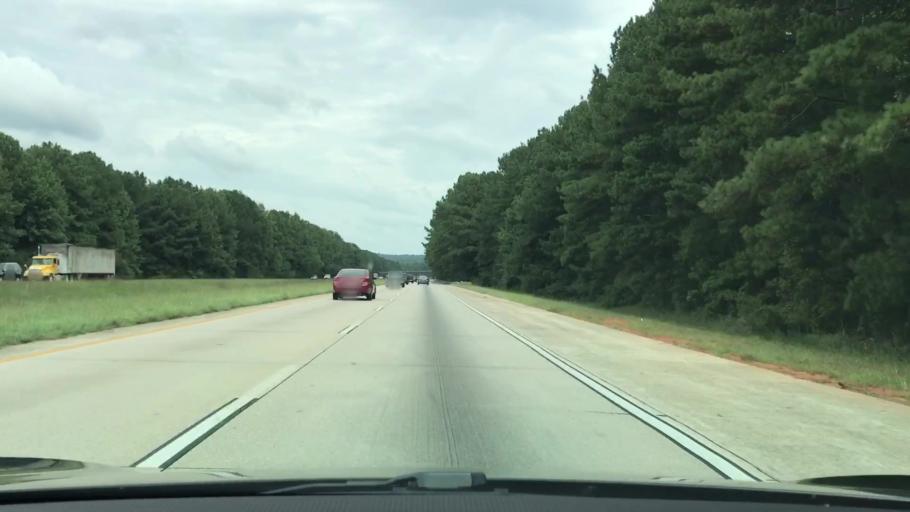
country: US
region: Georgia
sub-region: Troup County
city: Hogansville
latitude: 33.1208
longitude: -84.8979
